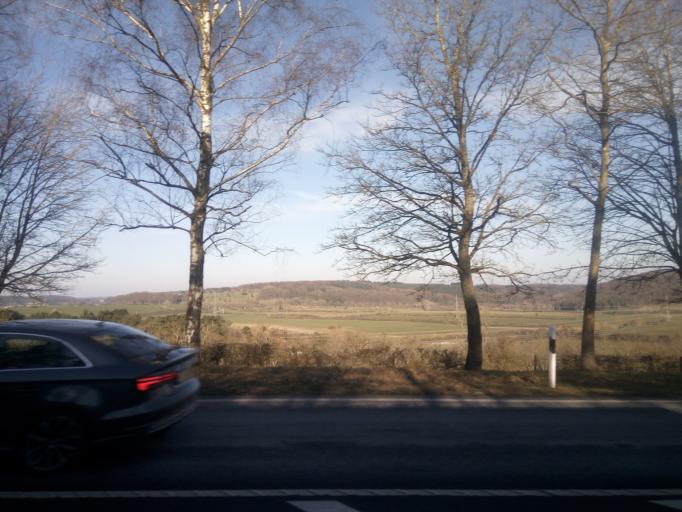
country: LU
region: Grevenmacher
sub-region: Canton de Grevenmacher
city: Junglinster
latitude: 49.7249
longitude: 6.2761
